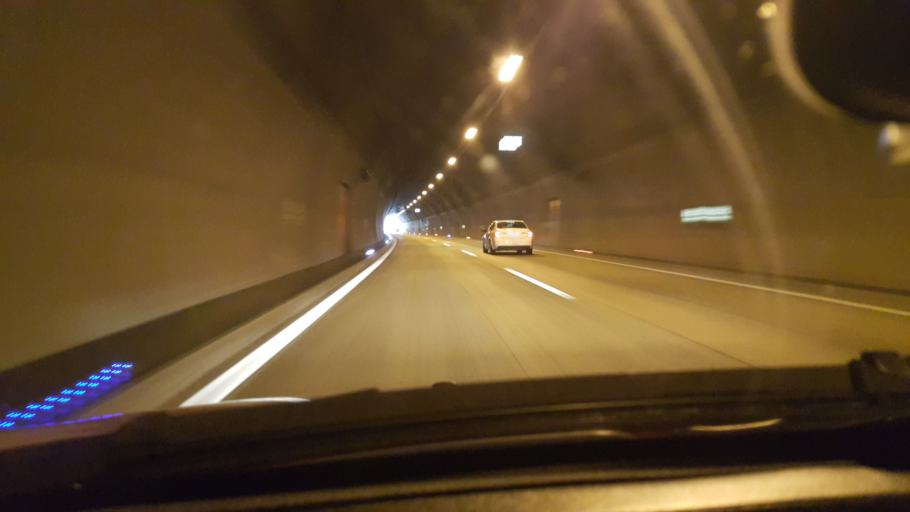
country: SI
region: Zagorje ob Savi
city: Izlake
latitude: 46.1841
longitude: 14.8644
